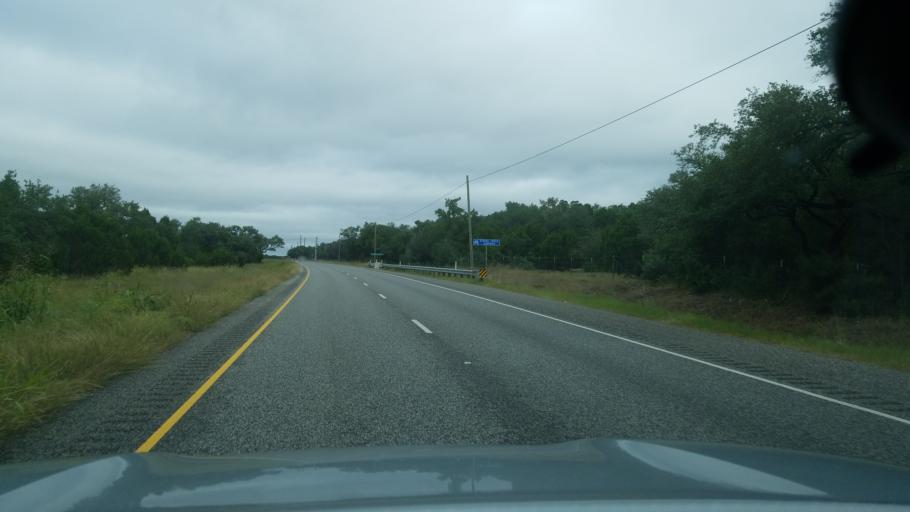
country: US
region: Texas
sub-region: Comal County
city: Canyon Lake
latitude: 29.9061
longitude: -98.4100
